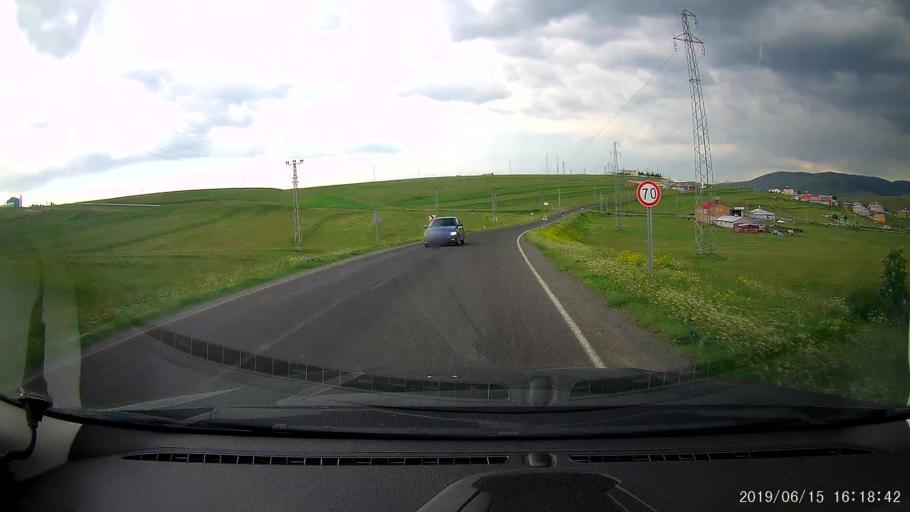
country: TR
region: Ardahan
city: Hanak
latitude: 41.2367
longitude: 42.8529
